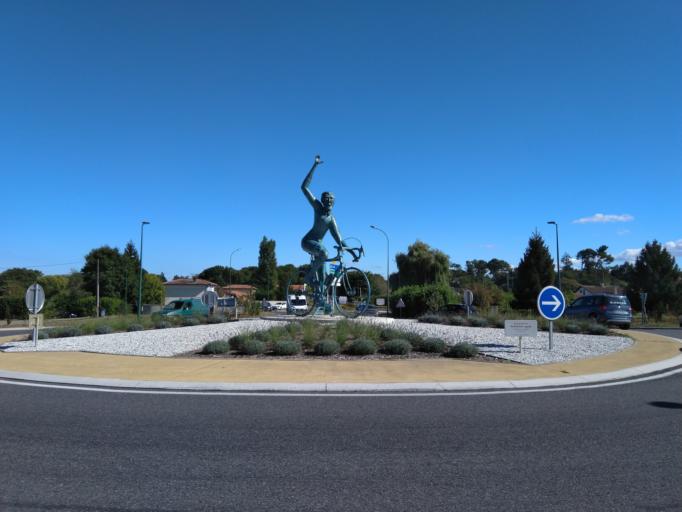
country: FR
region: Aquitaine
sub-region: Departement des Landes
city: Narrosse
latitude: 43.6977
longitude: -1.0219
